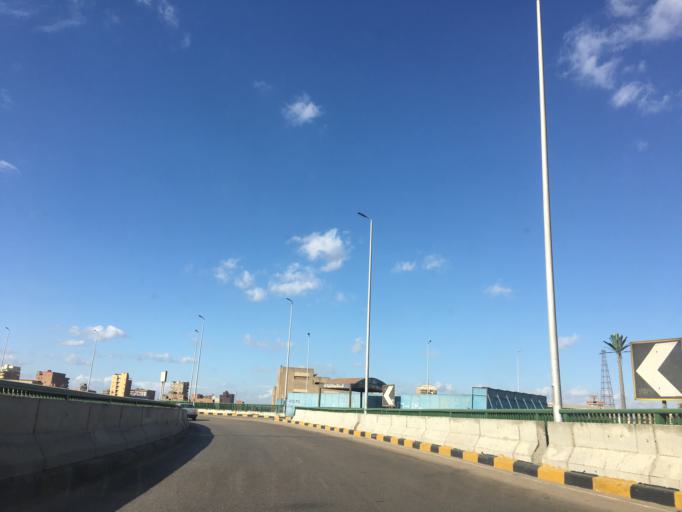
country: EG
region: Al Jizah
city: Al Jizah
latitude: 30.0282
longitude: 31.2000
